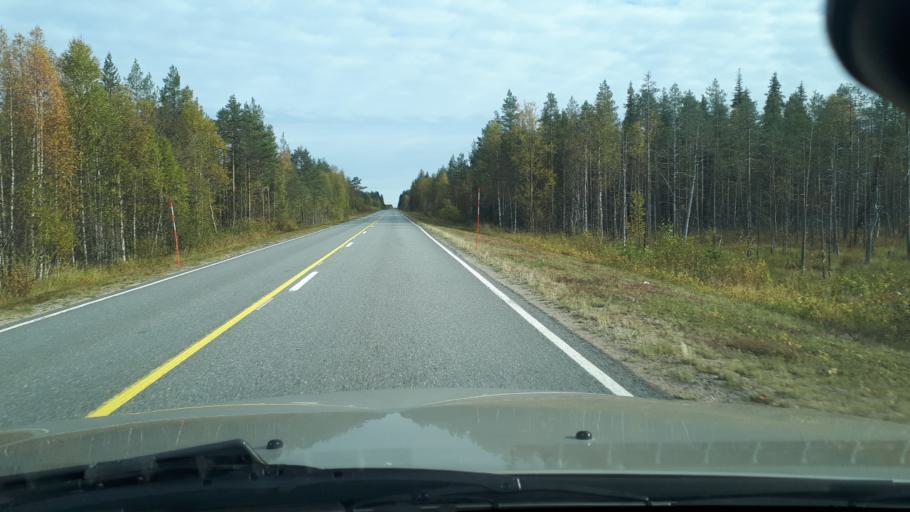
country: FI
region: Lapland
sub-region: Rovaniemi
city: Ranua
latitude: 65.9622
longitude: 26.0730
